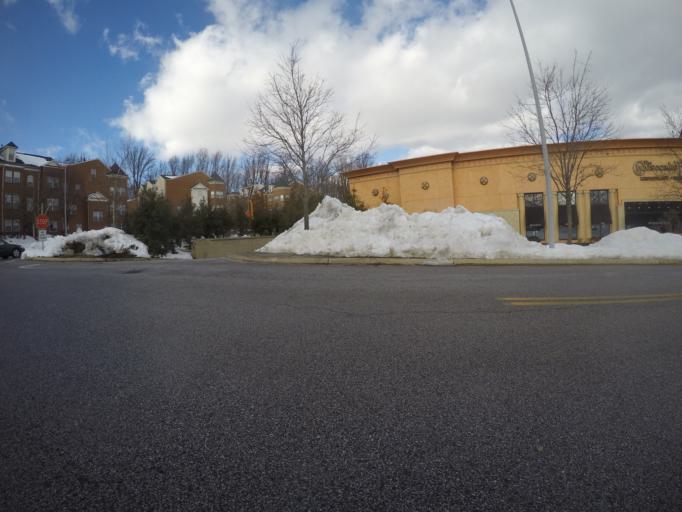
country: US
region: Maryland
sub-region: Howard County
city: Columbia
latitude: 39.2167
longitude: -76.8645
